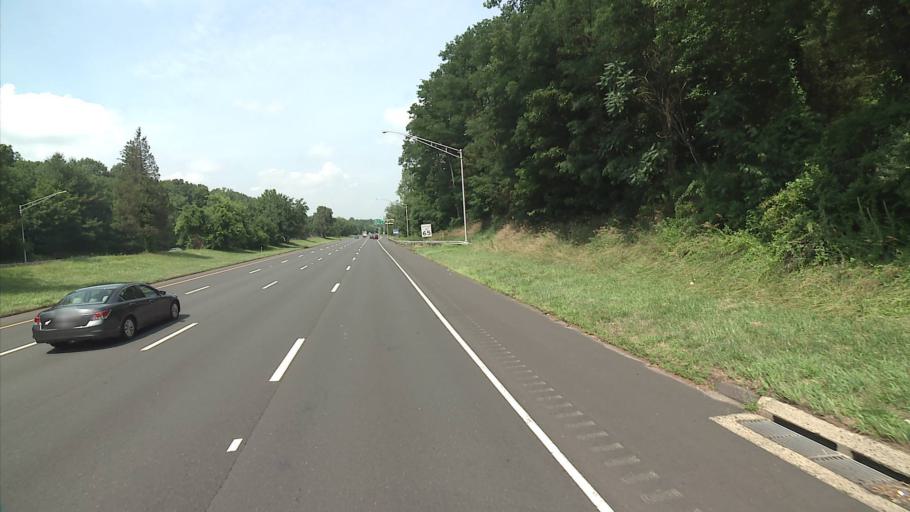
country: US
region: Connecticut
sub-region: Hartford County
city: Manchester
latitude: 41.7631
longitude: -72.5316
